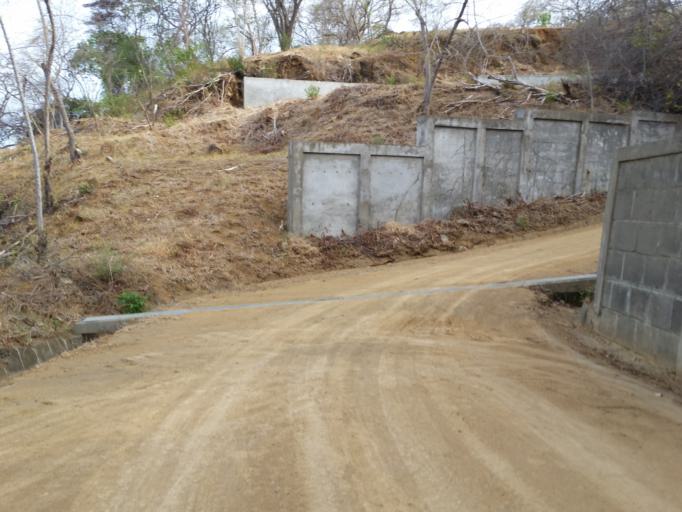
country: NI
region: Rivas
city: Tola
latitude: 11.4369
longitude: -86.0847
